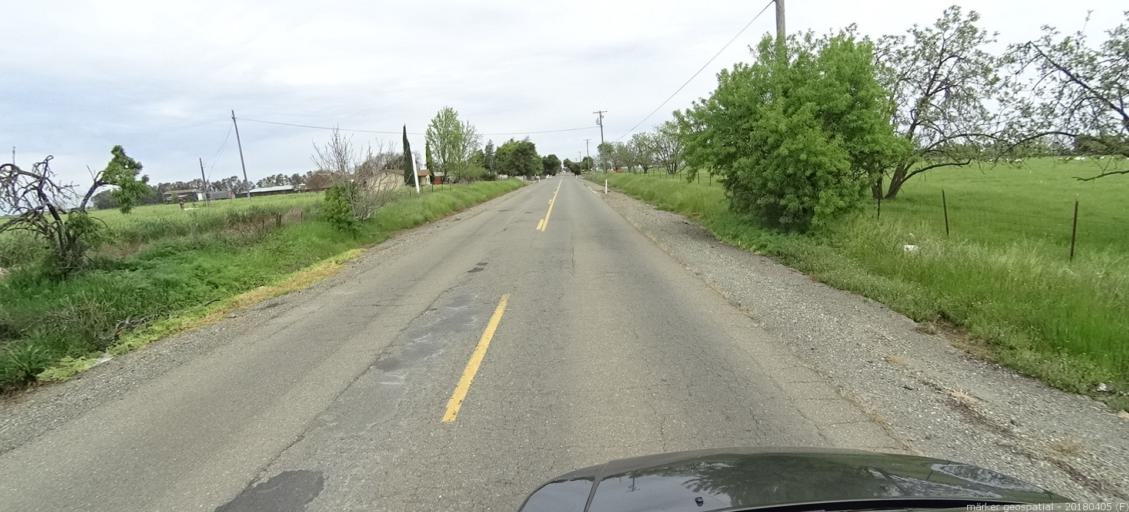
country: US
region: California
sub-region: Sacramento County
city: Galt
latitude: 38.2820
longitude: -121.3374
